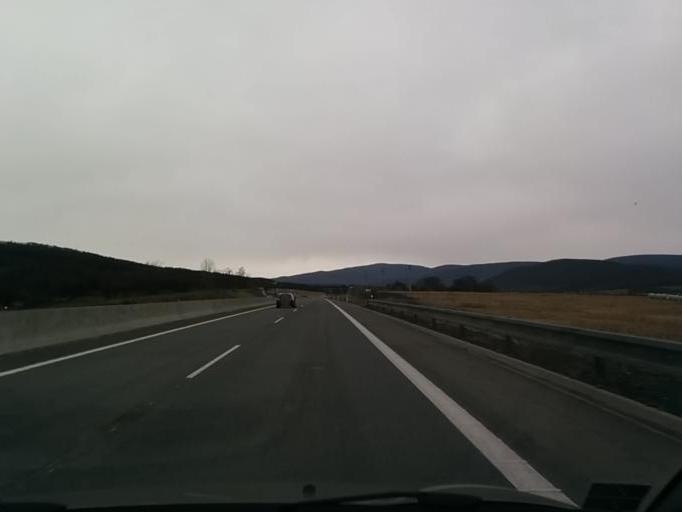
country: SK
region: Nitriansky
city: Tlmace
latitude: 48.3723
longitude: 18.5238
